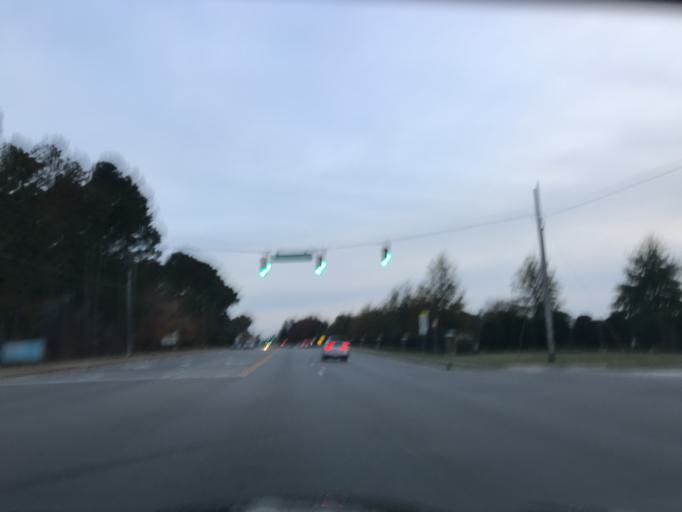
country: US
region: North Carolina
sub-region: Wake County
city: West Raleigh
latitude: 35.8854
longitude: -78.6272
